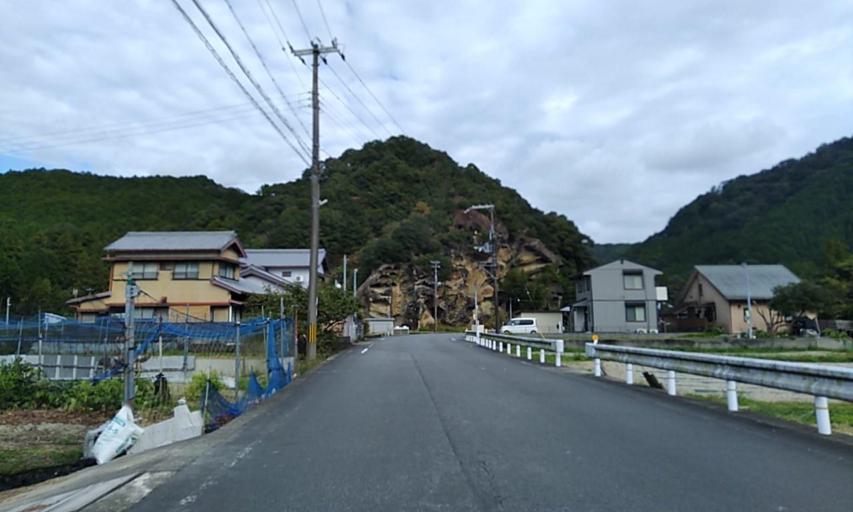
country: JP
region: Wakayama
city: Shingu
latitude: 33.5393
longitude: 135.8245
